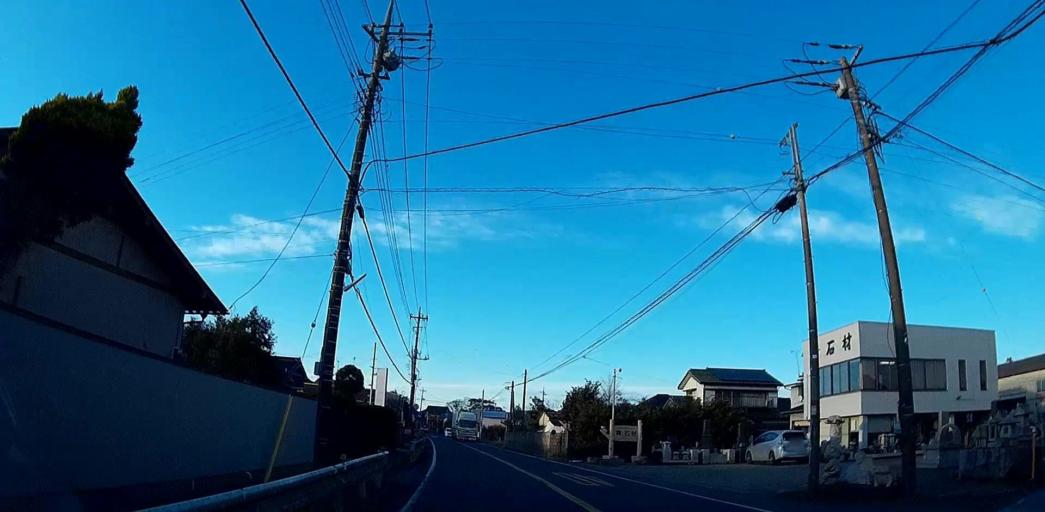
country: JP
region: Chiba
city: Omigawa
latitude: 35.8637
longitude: 140.5972
